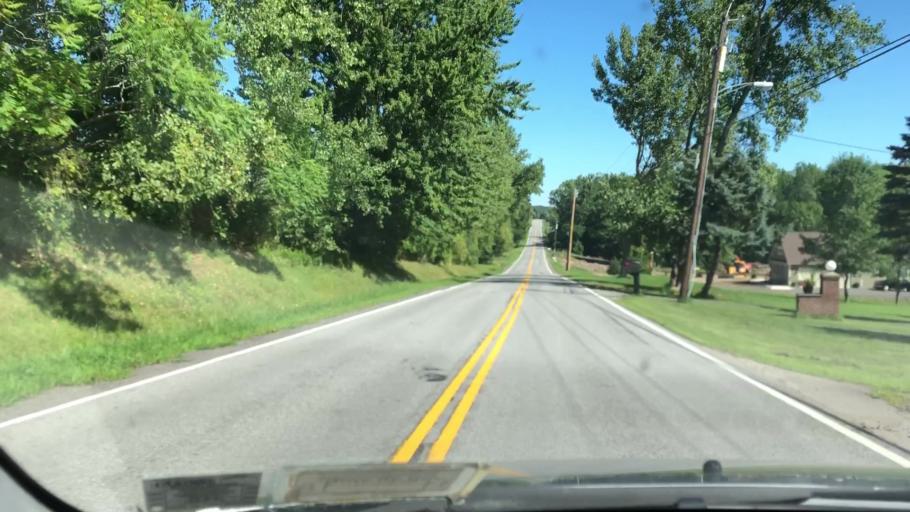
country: US
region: New York
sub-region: Monroe County
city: Fairport
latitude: 43.1115
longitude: -77.3730
